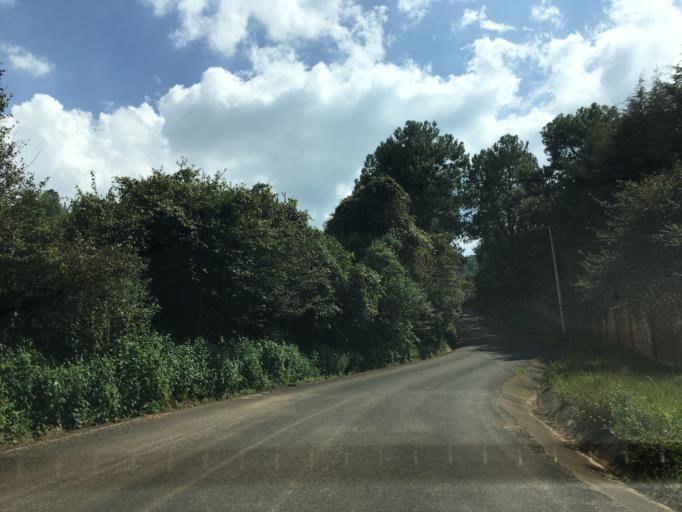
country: MX
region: Michoacan
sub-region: Morelia
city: Montana Monarca (Punta Altozano)
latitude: 19.5704
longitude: -101.1885
